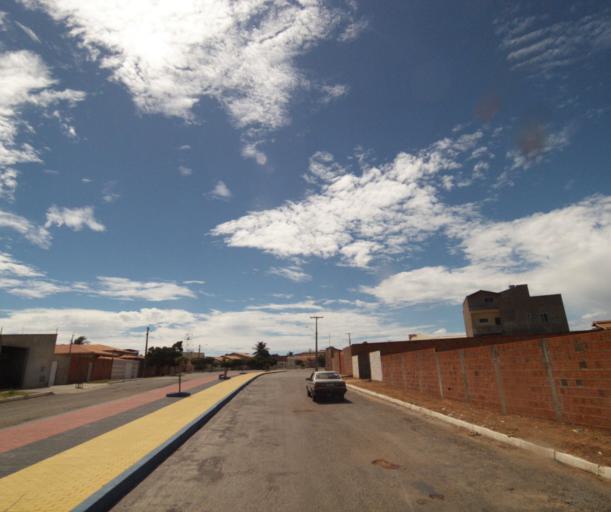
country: BR
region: Bahia
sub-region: Guanambi
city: Guanambi
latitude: -14.2387
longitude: -42.7749
